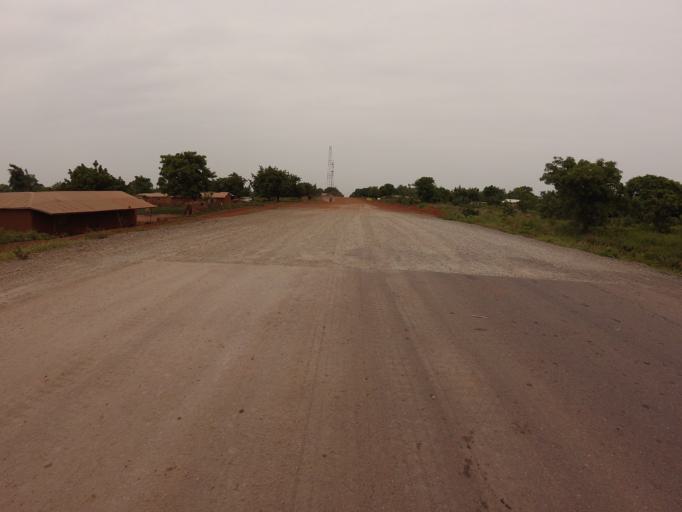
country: GH
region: Northern
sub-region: Yendi
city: Yendi
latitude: 9.2875
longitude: 0.0180
